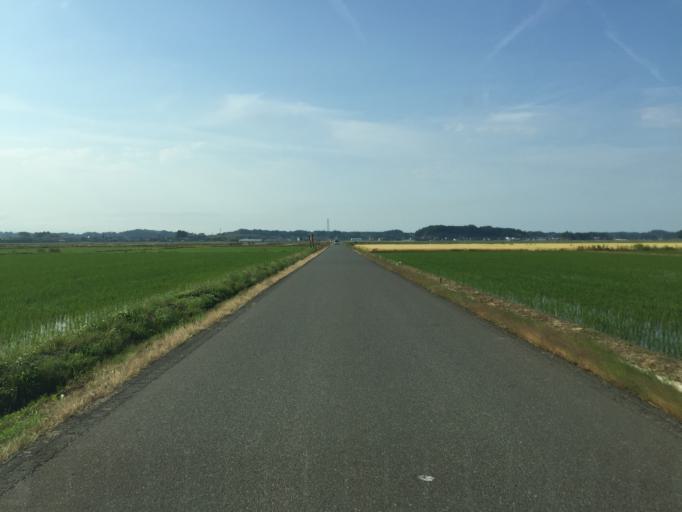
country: JP
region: Miyagi
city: Marumori
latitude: 37.7924
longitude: 140.9490
